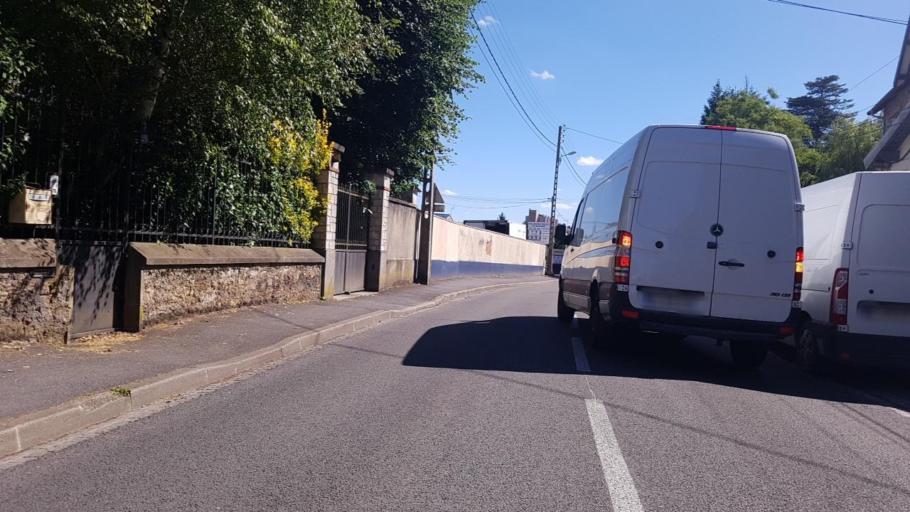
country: FR
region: Ile-de-France
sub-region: Departement de Seine-et-Marne
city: Meaux
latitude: 48.9512
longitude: 2.8706
